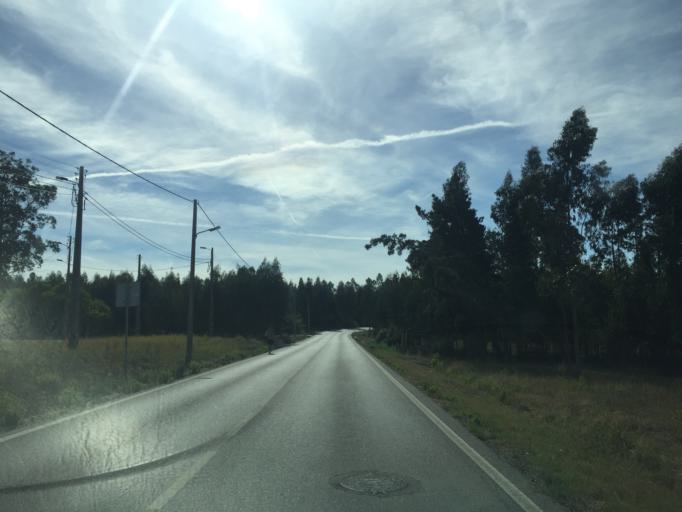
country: PT
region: Coimbra
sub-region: Figueira da Foz
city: Lavos
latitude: 40.0842
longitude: -8.8240
